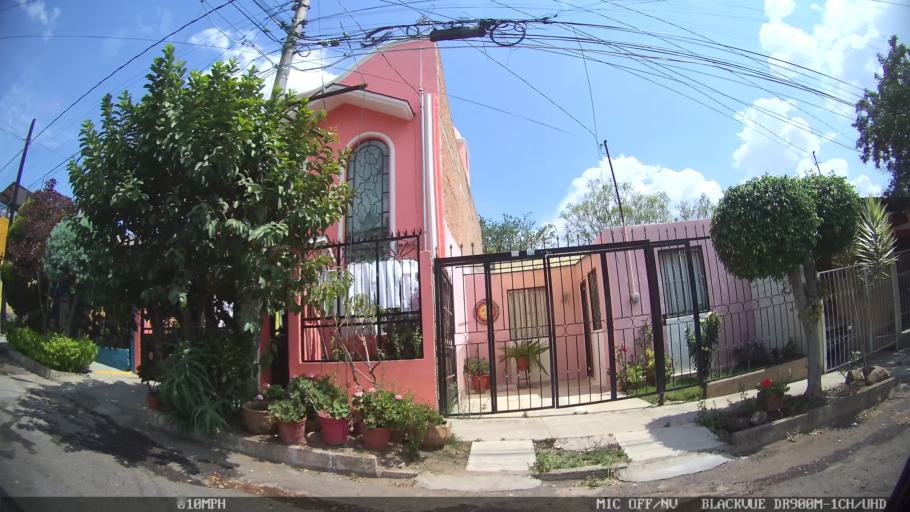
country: MX
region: Jalisco
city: Tonala
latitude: 20.6227
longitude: -103.2512
